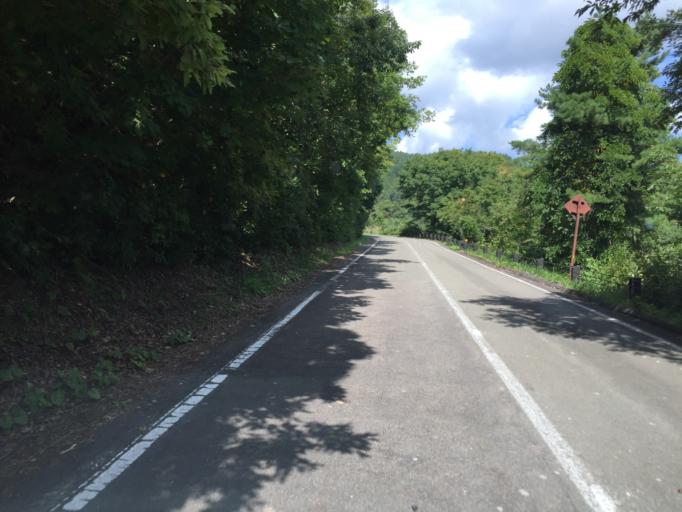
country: JP
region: Fukushima
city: Inawashiro
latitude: 37.5884
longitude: 140.0296
